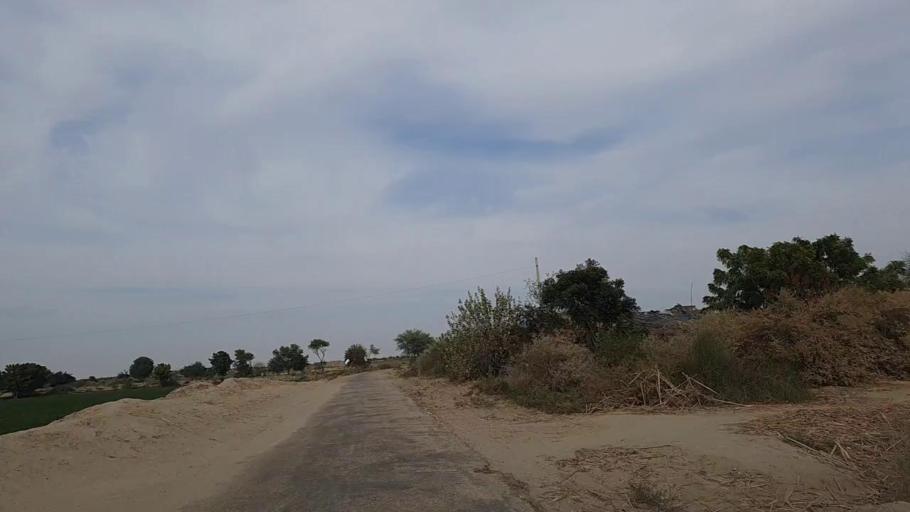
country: PK
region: Sindh
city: Jam Sahib
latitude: 26.4446
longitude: 68.6122
